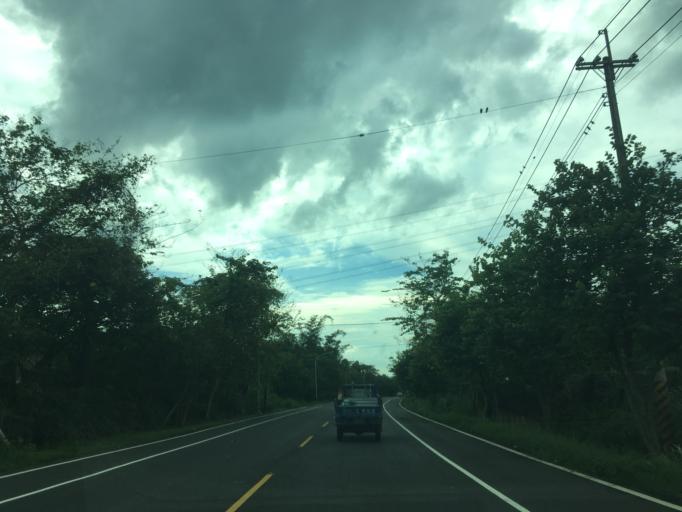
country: TW
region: Taiwan
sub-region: Chiayi
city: Jiayi Shi
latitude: 23.4417
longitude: 120.5970
